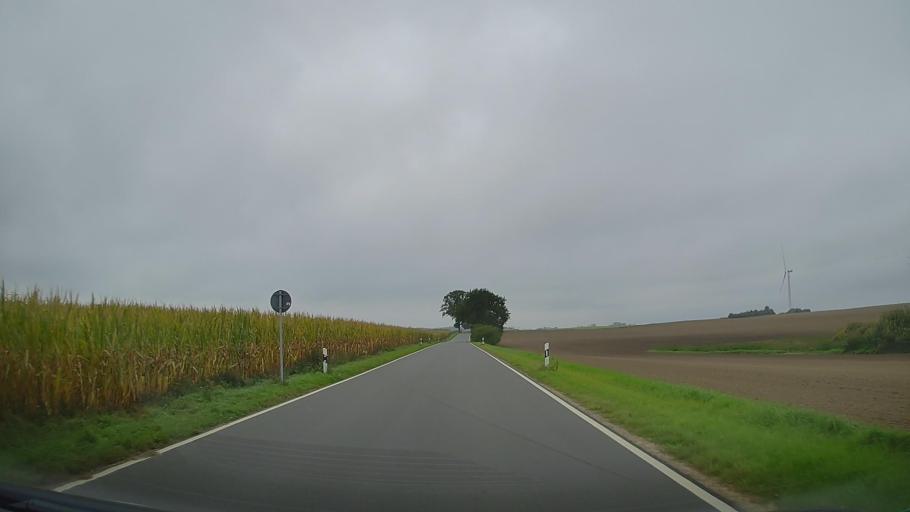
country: DE
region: Mecklenburg-Vorpommern
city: Dummerstorf
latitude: 53.9674
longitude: 12.2453
